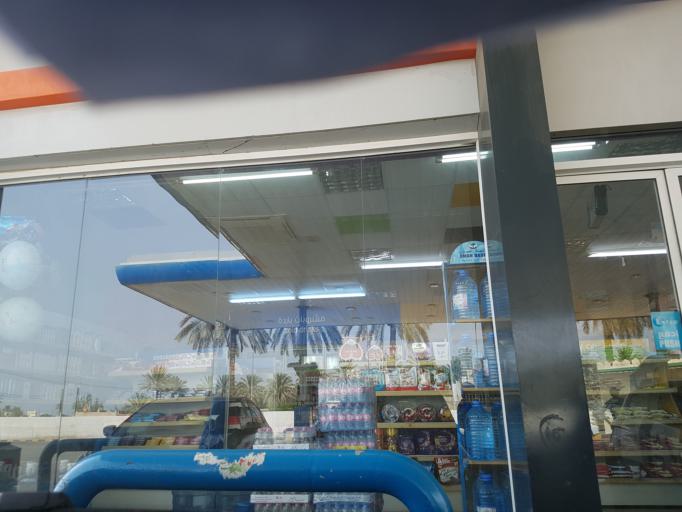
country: OM
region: Al Batinah
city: Barka'
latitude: 23.7121
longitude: 57.7503
